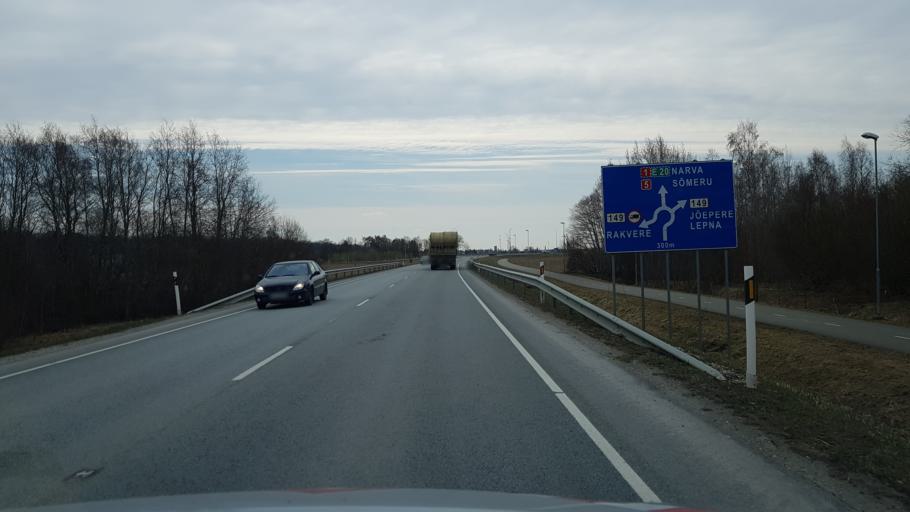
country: EE
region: Laeaene-Virumaa
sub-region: Rakvere linn
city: Rakvere
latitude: 59.3432
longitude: 26.3418
